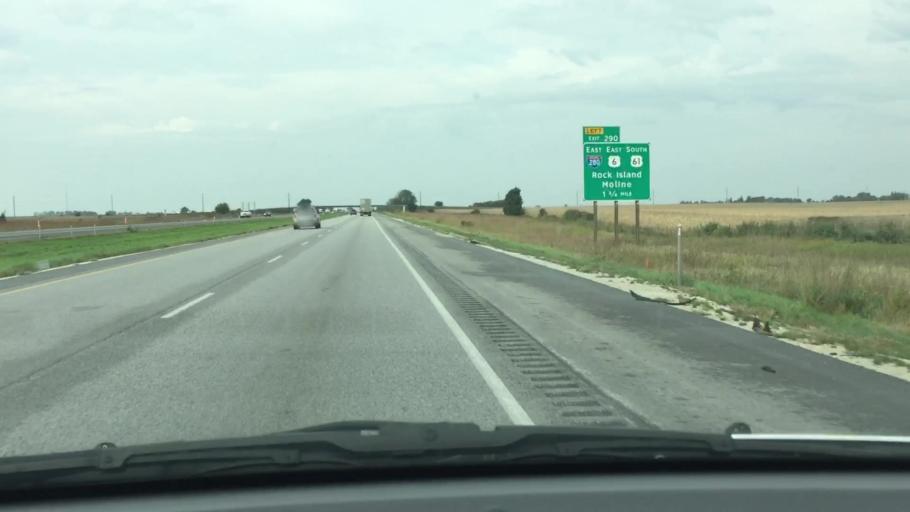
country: US
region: Iowa
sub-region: Scott County
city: Eldridge
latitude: 41.6007
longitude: -90.6362
